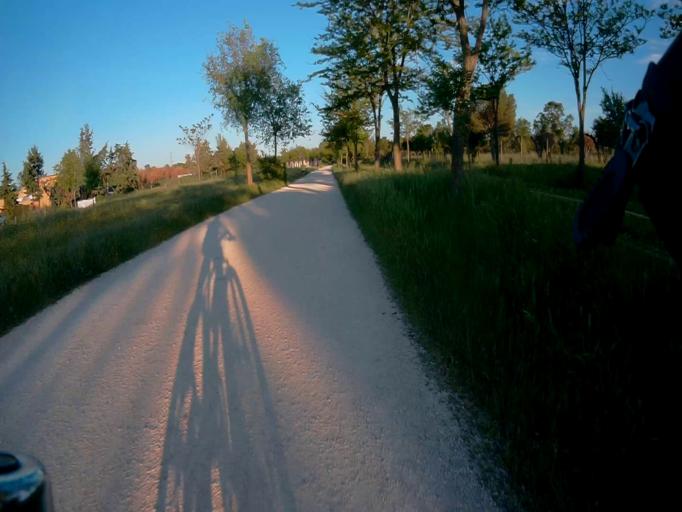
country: ES
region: Madrid
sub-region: Provincia de Madrid
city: Alcorcon
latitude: 40.3288
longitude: -3.7982
